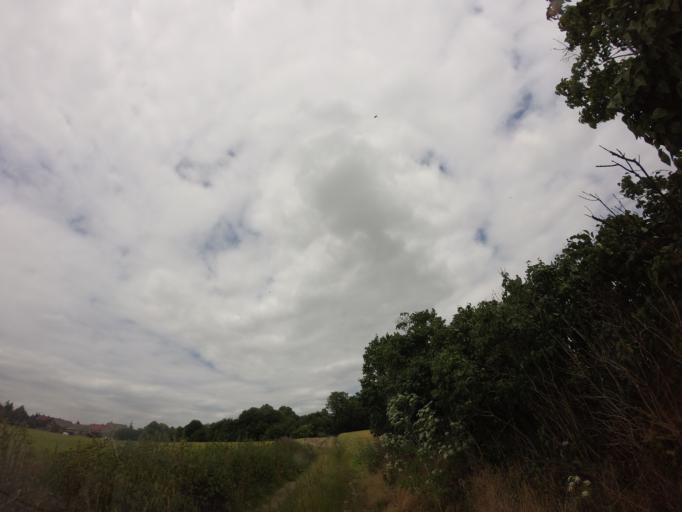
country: PL
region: West Pomeranian Voivodeship
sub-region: Powiat choszczenski
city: Krzecin
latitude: 53.0728
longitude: 15.5271
